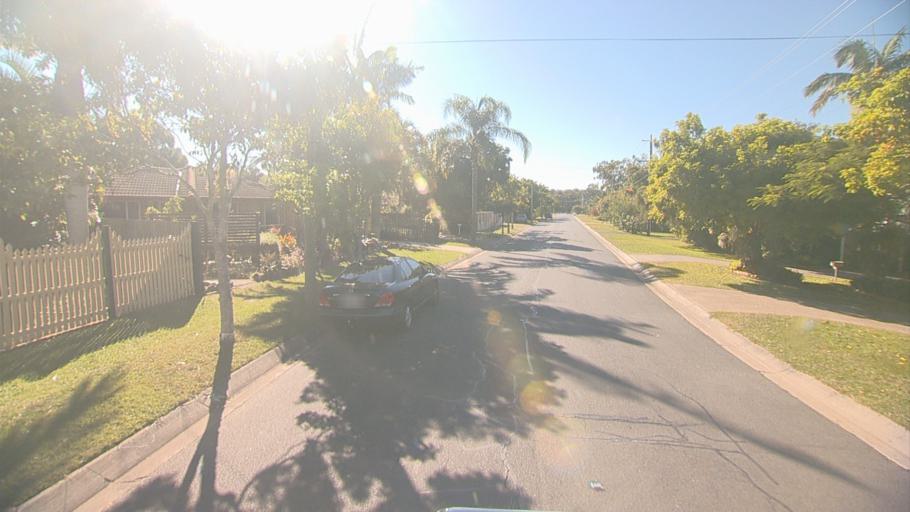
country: AU
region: Queensland
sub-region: Logan
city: Slacks Creek
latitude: -27.6521
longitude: 153.1563
